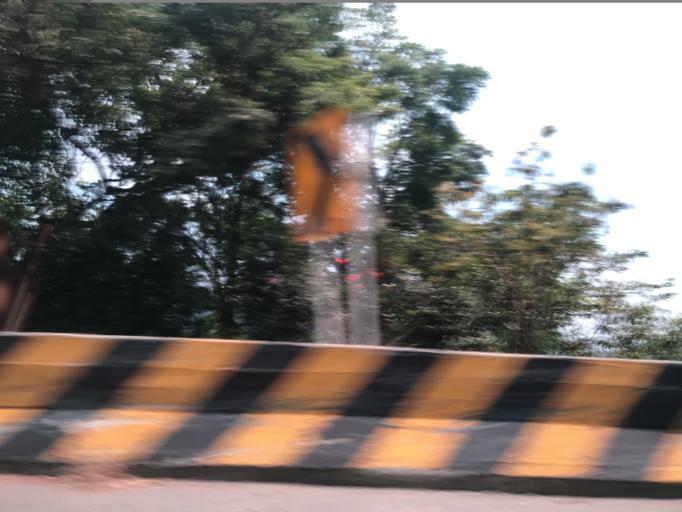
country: CO
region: Valle del Cauca
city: Cali
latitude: 3.4803
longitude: -76.6009
